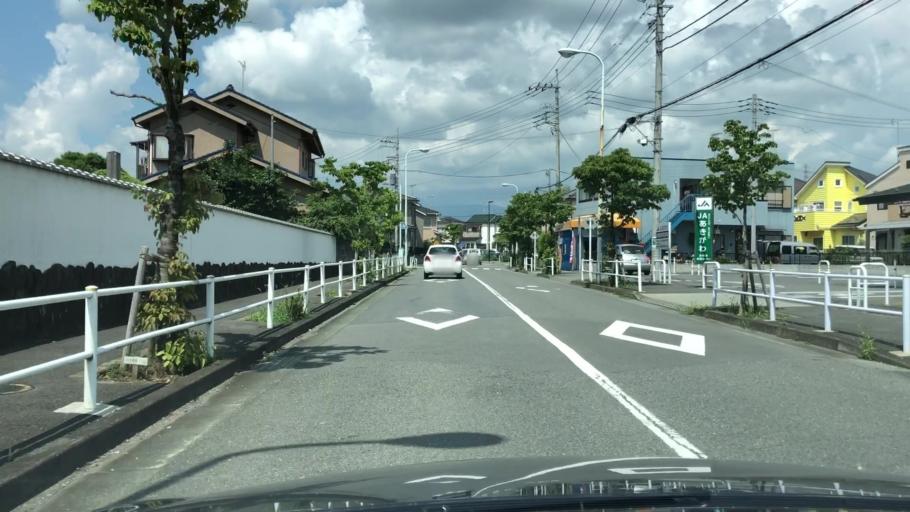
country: JP
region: Tokyo
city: Fussa
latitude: 35.7230
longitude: 139.2756
